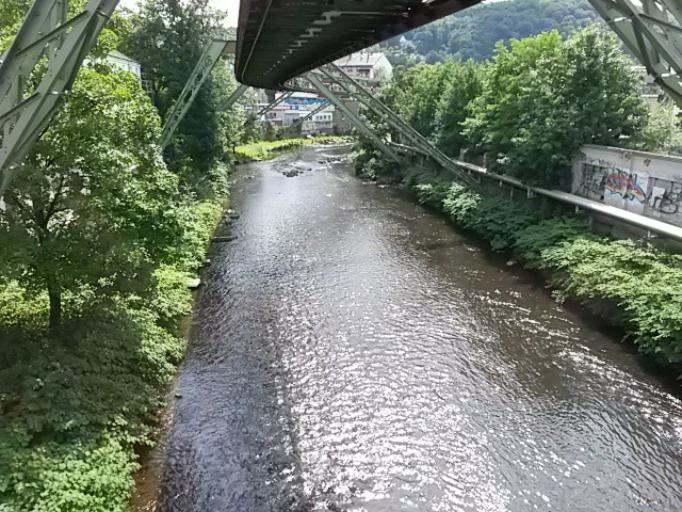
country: DE
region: North Rhine-Westphalia
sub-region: Regierungsbezirk Dusseldorf
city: Wuppertal
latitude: 51.2506
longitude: 7.1316
